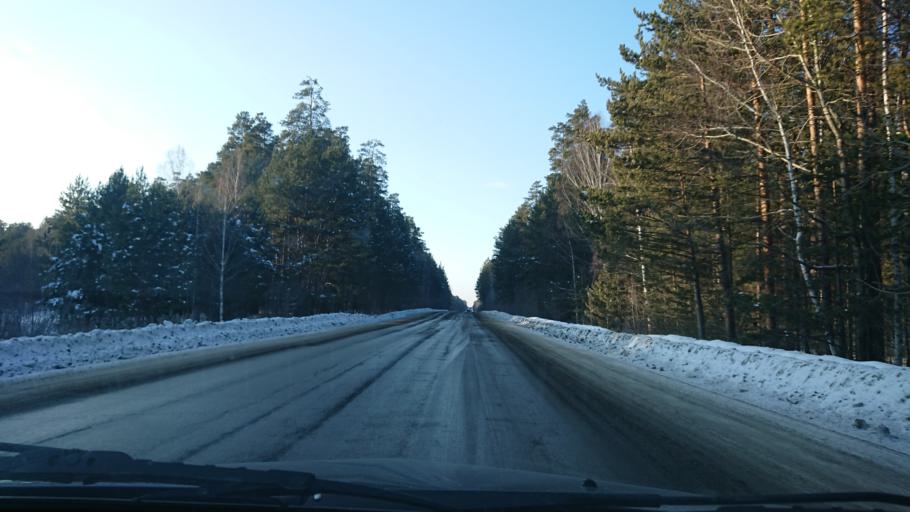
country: RU
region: Sverdlovsk
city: Gornyy Shchit
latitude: 56.6261
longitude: 60.3499
